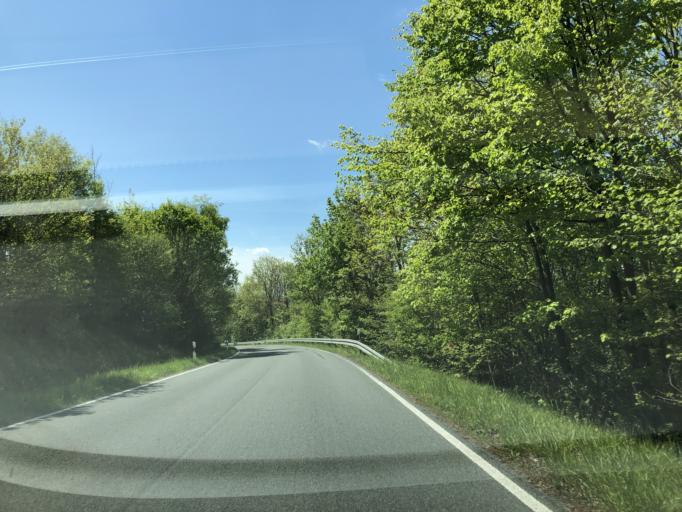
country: DE
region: Hesse
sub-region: Regierungsbezirk Kassel
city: Grossalmerode
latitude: 51.2475
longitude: 9.8435
